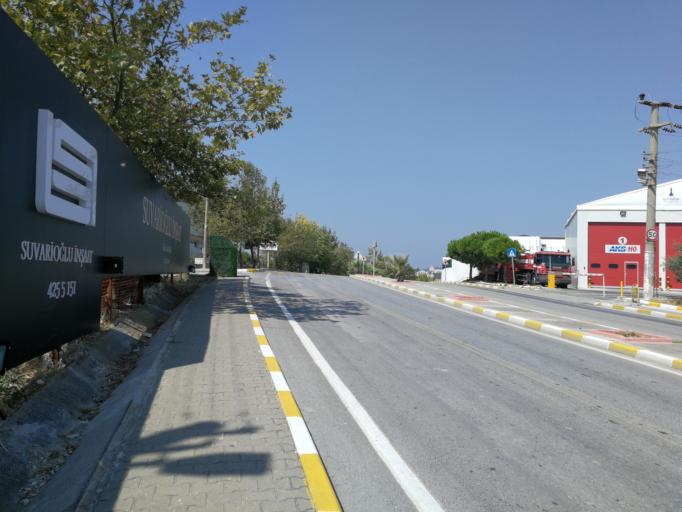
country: TR
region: Izmir
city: Urla
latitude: 38.3267
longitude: 26.7715
